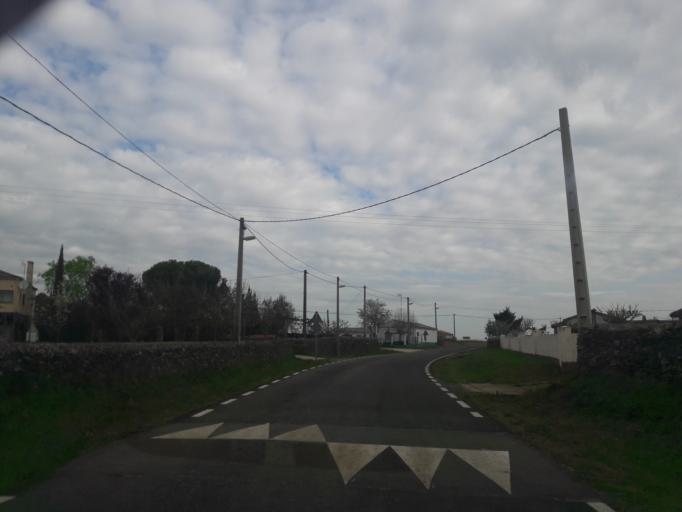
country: ES
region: Castille and Leon
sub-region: Provincia de Salamanca
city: Pastores
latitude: 40.5007
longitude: -6.5311
